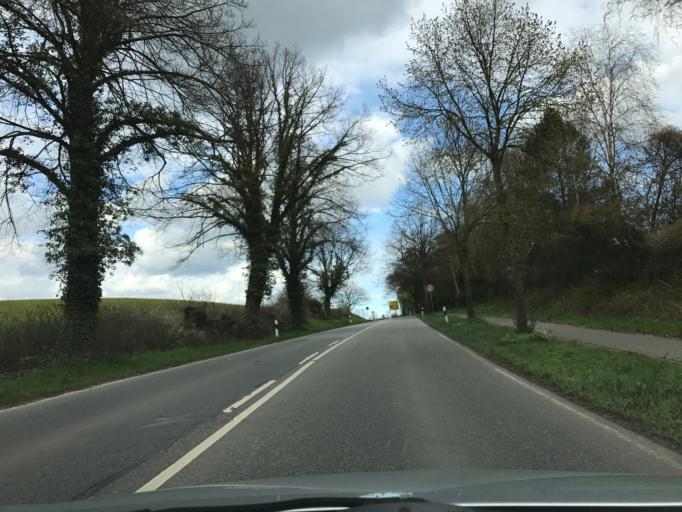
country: DE
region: Schleswig-Holstein
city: Altenkrempe
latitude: 54.1170
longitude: 10.8383
